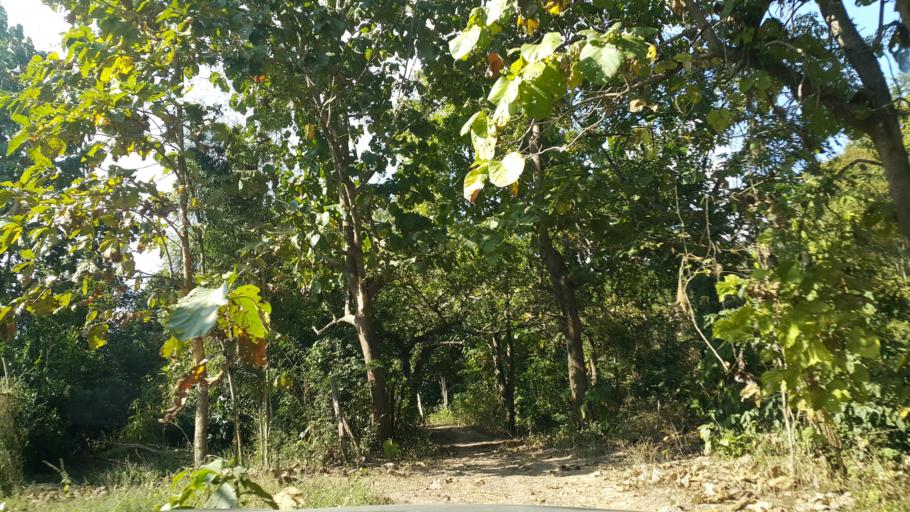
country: TH
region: Lamphun
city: Ban Thi
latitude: 18.5729
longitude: 99.1735
